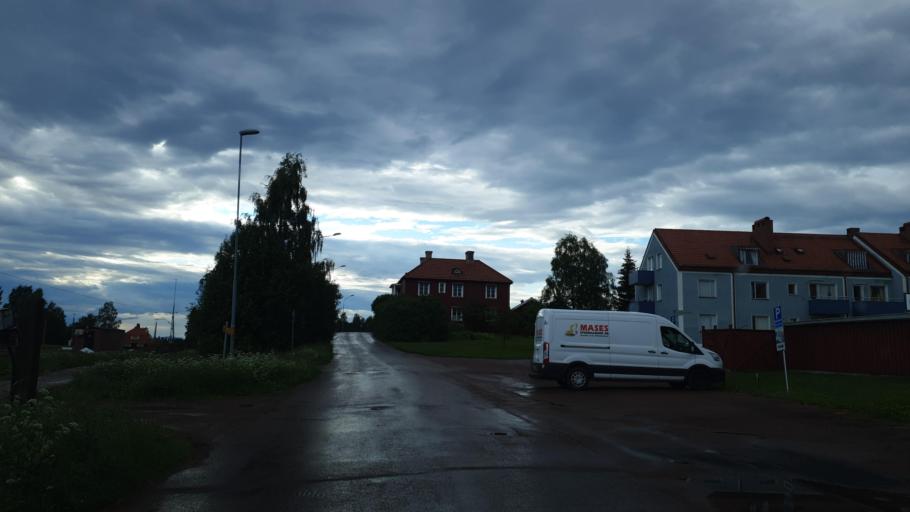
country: SE
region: Dalarna
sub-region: Mora Kommun
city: Mora
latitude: 61.0031
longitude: 14.5808
